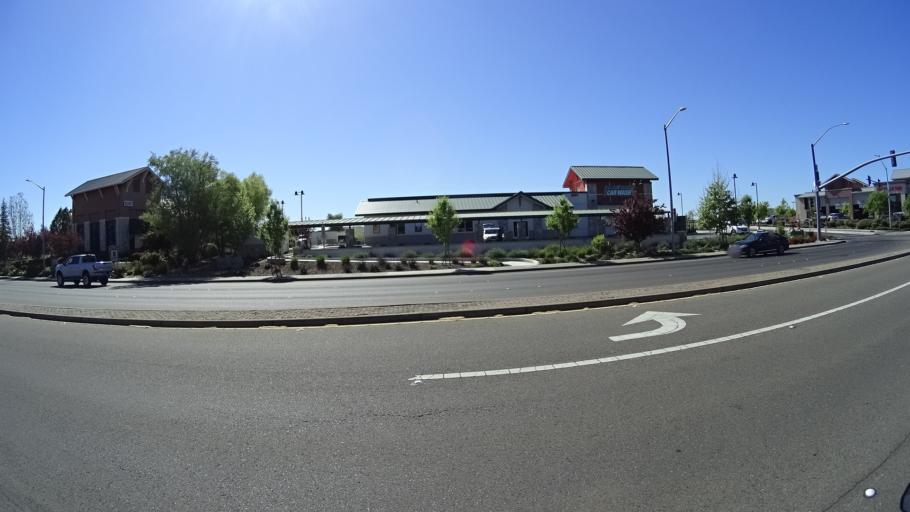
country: US
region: California
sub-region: Placer County
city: Rocklin
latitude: 38.7943
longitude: -121.2680
